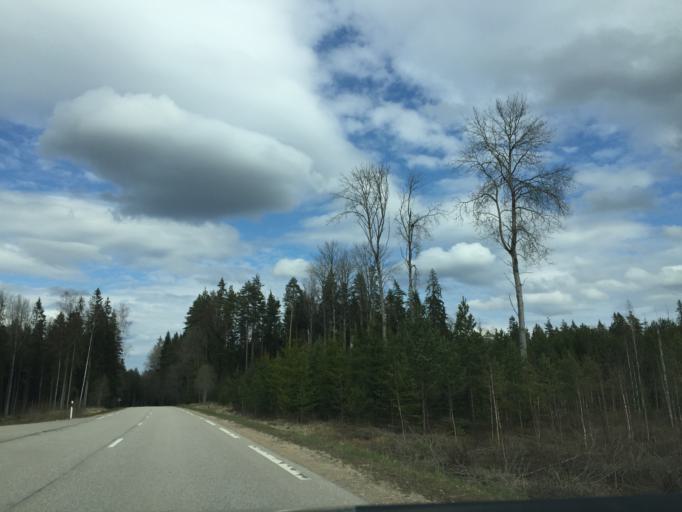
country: LV
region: Jaunpiebalga
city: Jaunpiebalga
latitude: 57.2275
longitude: 26.2348
